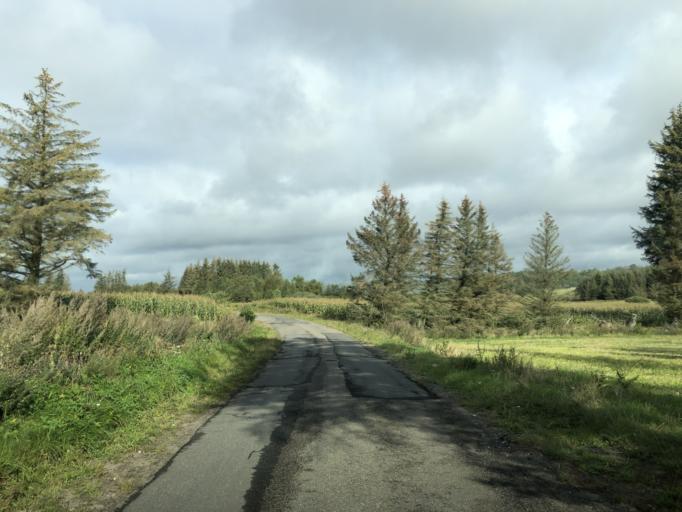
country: DK
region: Central Jutland
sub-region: Holstebro Kommune
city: Ulfborg
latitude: 56.2935
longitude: 8.4543
